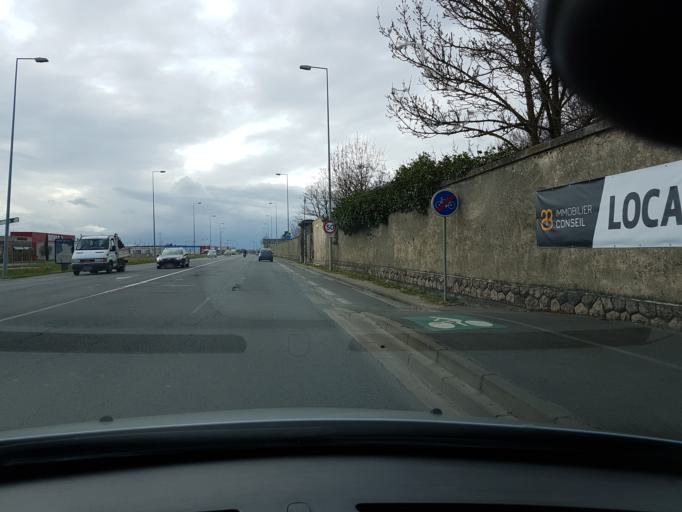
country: FR
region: Centre
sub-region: Departement du Cher
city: Bourges
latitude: 47.0962
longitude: 2.4404
